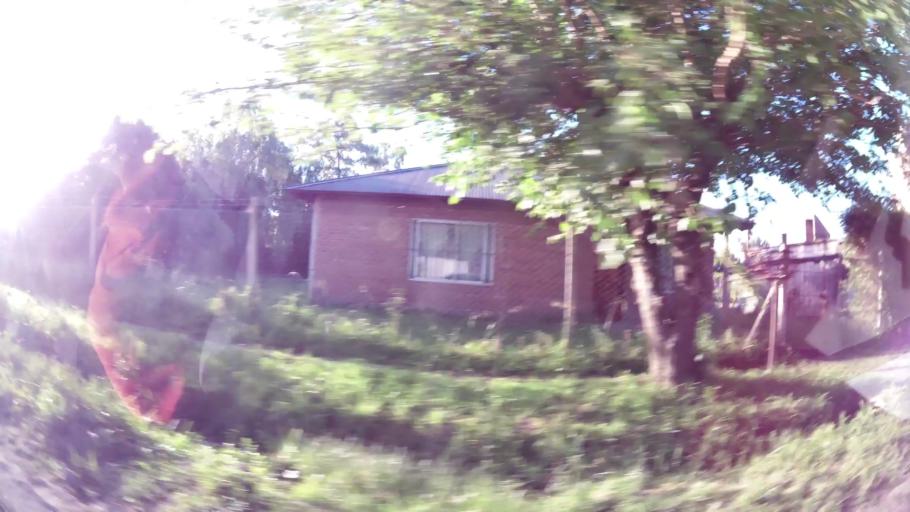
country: AR
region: Buenos Aires
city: Santa Catalina - Dique Lujan
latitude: -34.4708
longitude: -58.7487
